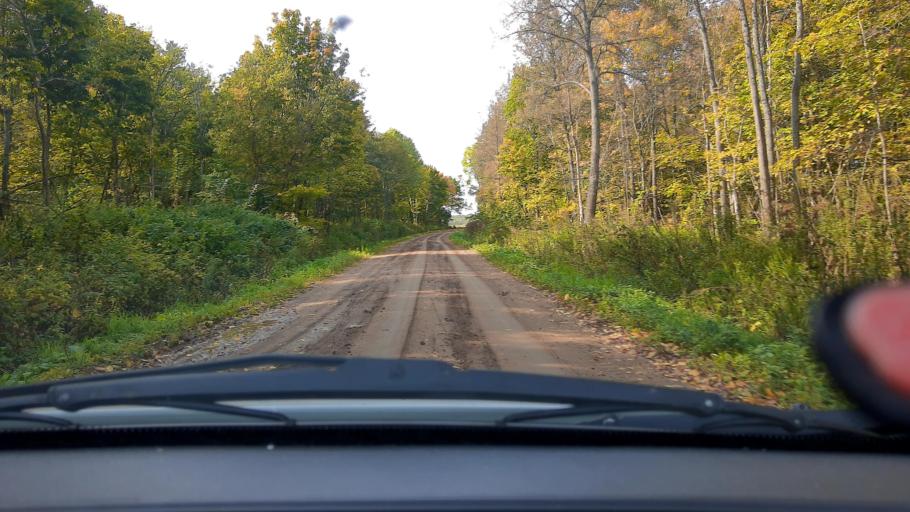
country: RU
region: Bashkortostan
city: Kudeyevskiy
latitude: 54.7120
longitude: 56.6450
